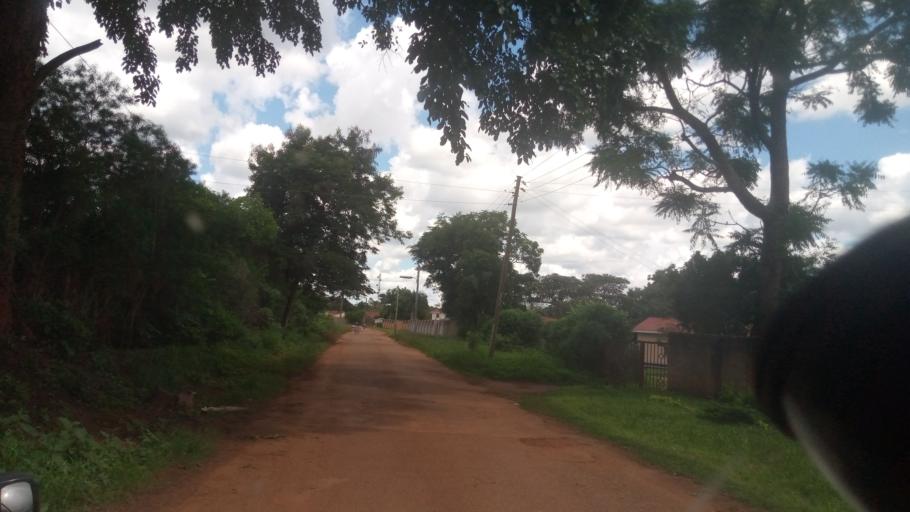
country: UG
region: Northern Region
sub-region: Lira District
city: Lira
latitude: 2.2433
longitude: 32.9030
